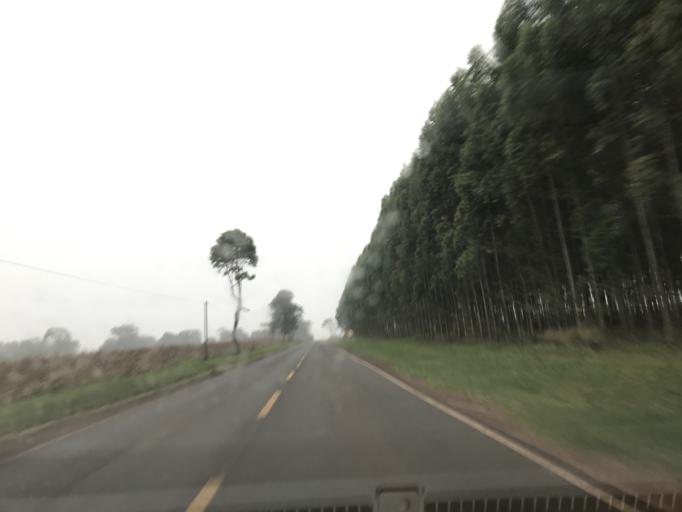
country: PY
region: Canindeyu
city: Salto del Guaira
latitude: -24.1131
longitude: -54.1125
